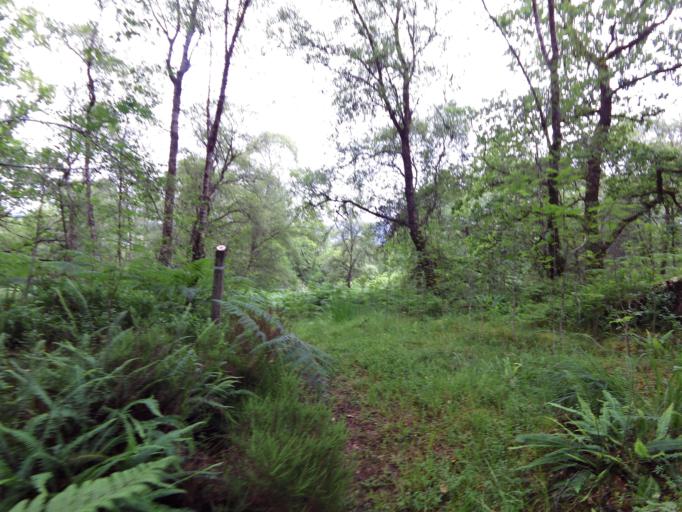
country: GB
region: Scotland
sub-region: Highland
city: Fort William
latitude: 56.8331
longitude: -5.1259
